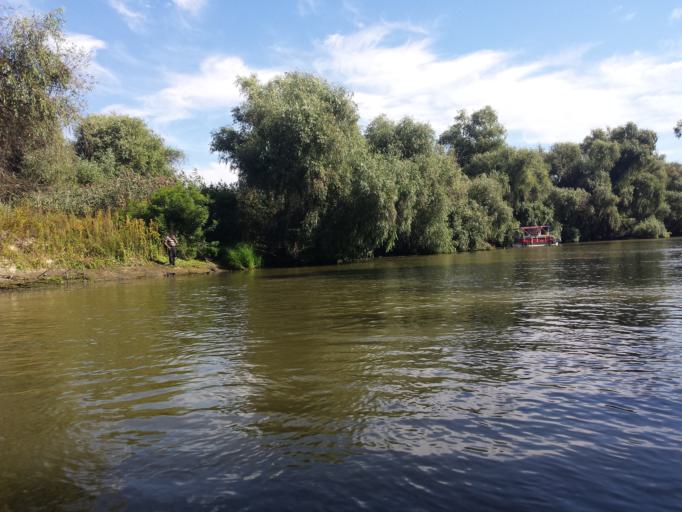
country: RO
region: Tulcea
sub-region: Comuna Mahmudia
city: Mahmudia
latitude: 45.2173
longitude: 29.1670
